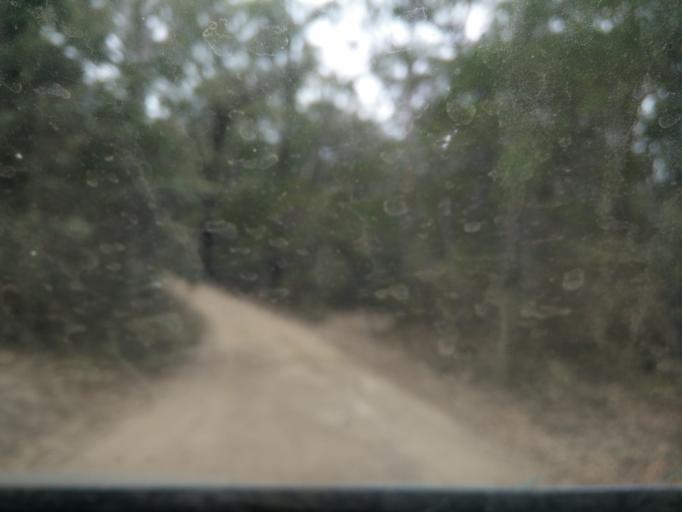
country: AU
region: New South Wales
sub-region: Penrith Municipality
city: Mulgoa
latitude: -33.8305
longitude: 150.5741
